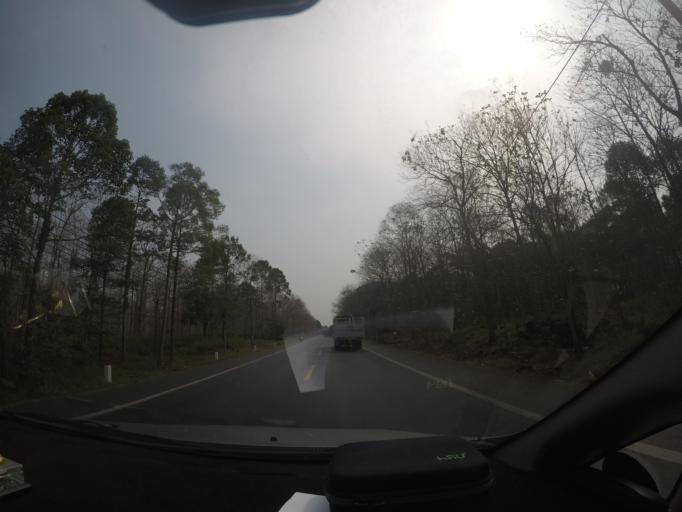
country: VN
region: Dong Nai
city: Tan Phu
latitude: 11.2435
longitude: 107.3963
